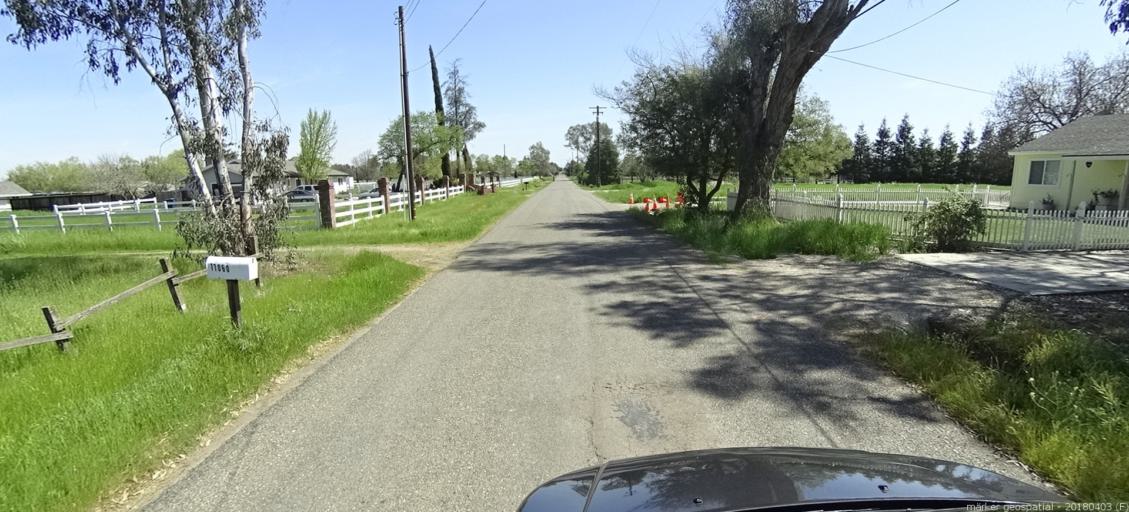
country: US
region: California
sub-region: Sacramento County
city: Wilton
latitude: 38.4021
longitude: -121.2710
